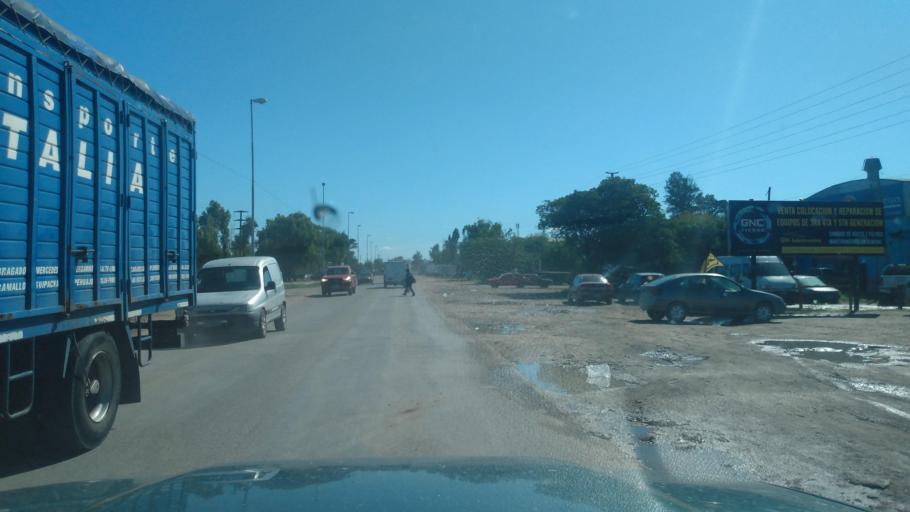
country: AR
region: Buenos Aires
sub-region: Partido de General Rodriguez
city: General Rodriguez
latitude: -34.5900
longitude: -58.9464
